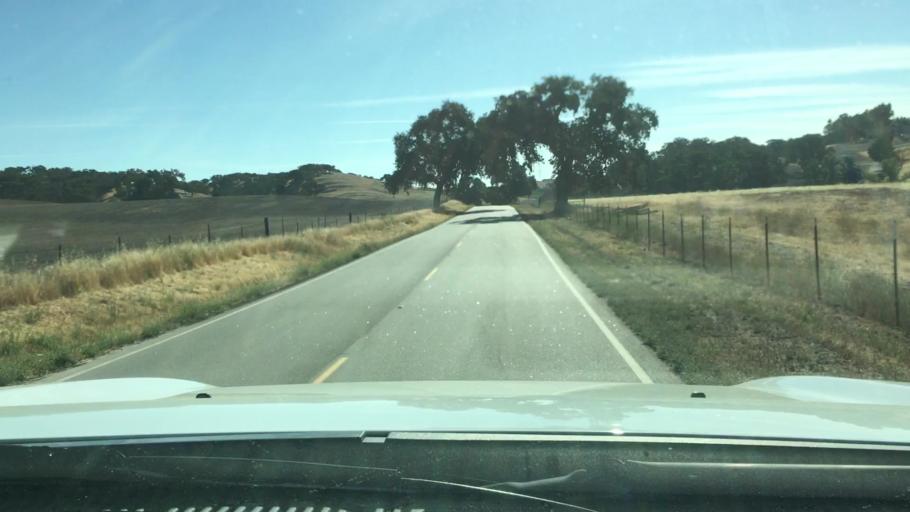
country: US
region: California
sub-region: San Luis Obispo County
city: Templeton
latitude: 35.5634
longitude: -120.6612
